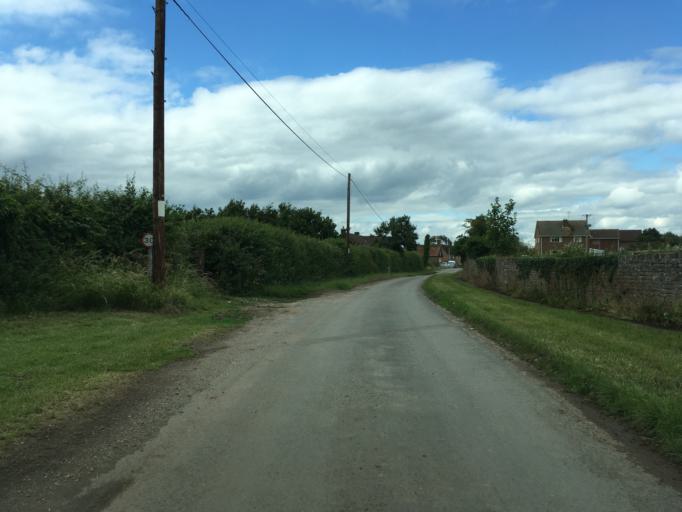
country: GB
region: England
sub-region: Gloucestershire
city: Cinderford
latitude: 51.7941
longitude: -2.4263
